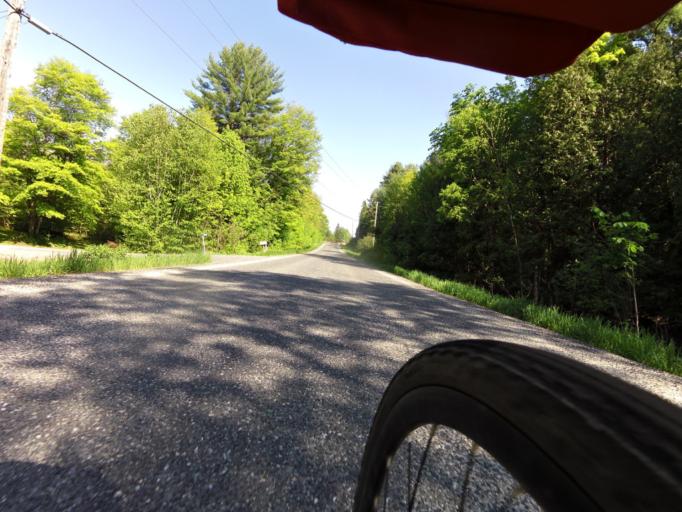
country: CA
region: Ontario
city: Renfrew
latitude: 45.1413
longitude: -76.5477
